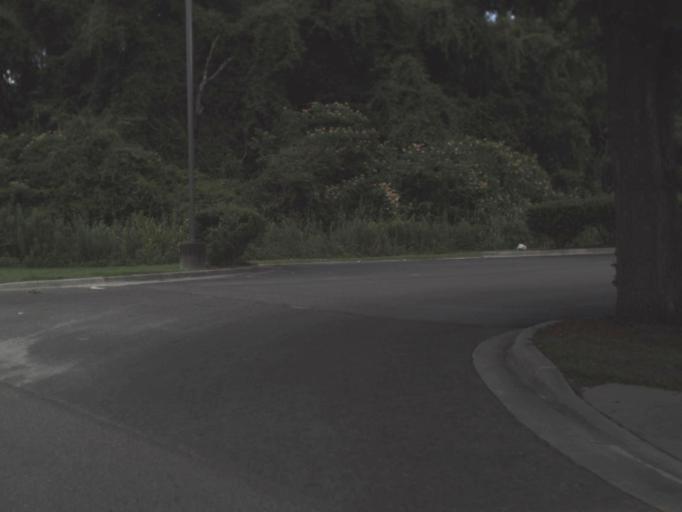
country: US
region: Florida
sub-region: Alachua County
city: Alachua
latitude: 29.6890
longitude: -82.4425
